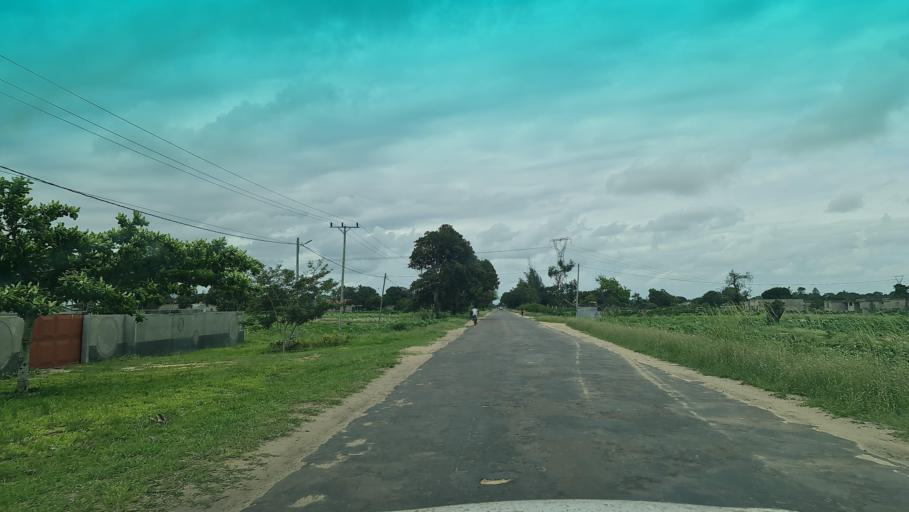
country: MZ
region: Maputo
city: Manhica
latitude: -25.4174
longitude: 32.7724
